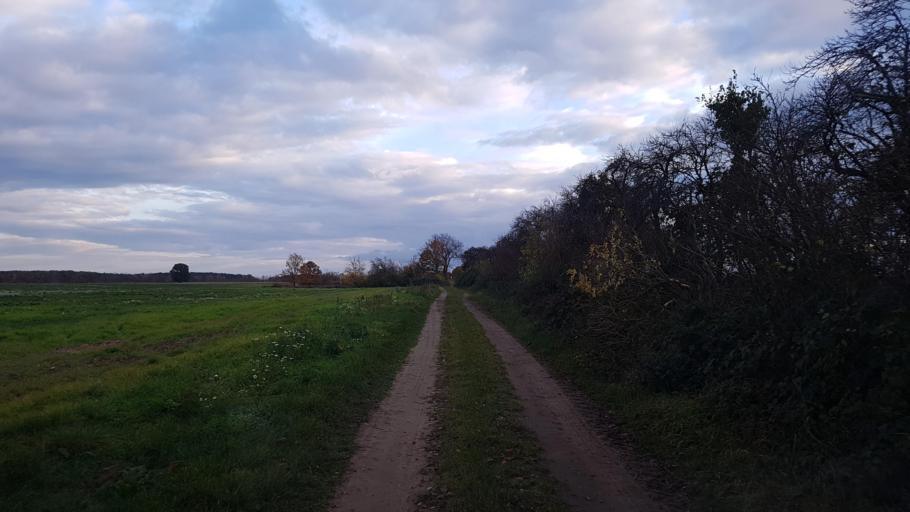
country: DE
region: Saxony-Anhalt
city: Seyda
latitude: 51.9430
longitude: 12.8721
